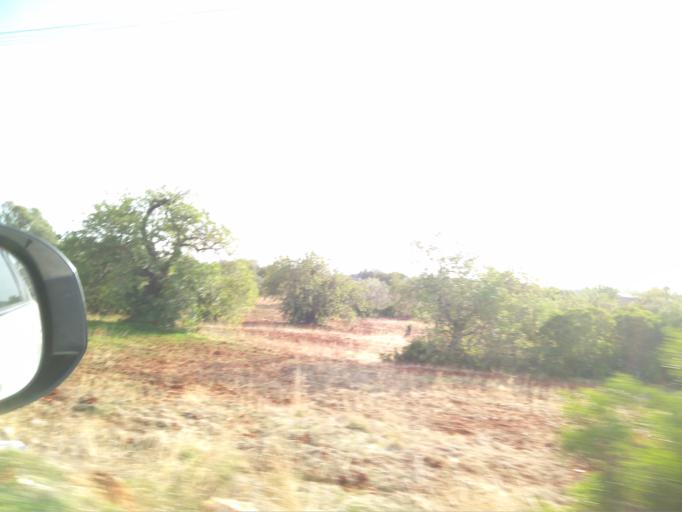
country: PT
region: Faro
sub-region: Faro
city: Santa Barbara de Nexe
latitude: 37.0973
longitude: -7.9541
